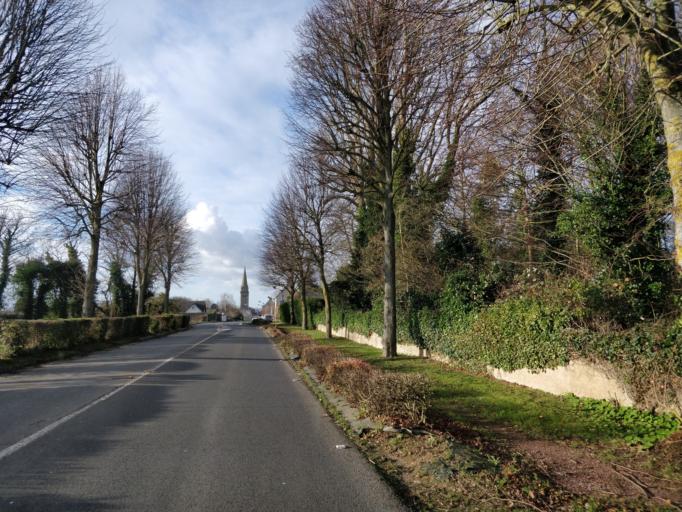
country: FR
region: Lower Normandy
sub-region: Departement du Calvados
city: Saint-Manvieu-Norrey
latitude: 49.2080
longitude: -0.5042
